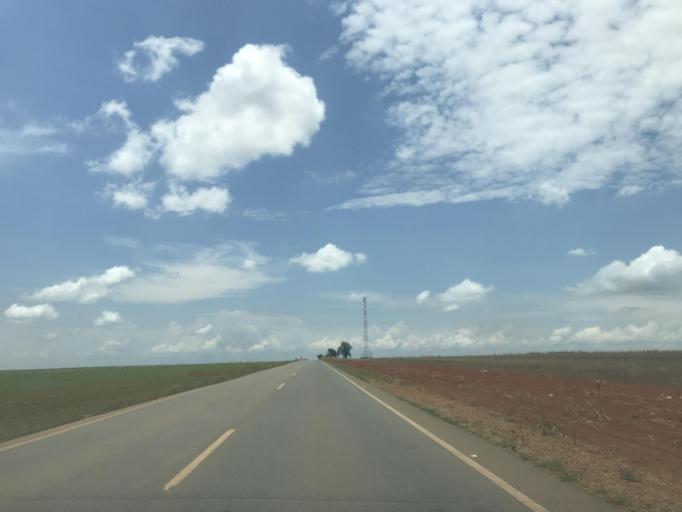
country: BR
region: Goias
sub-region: Vianopolis
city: Vianopolis
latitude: -16.5320
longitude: -48.2474
